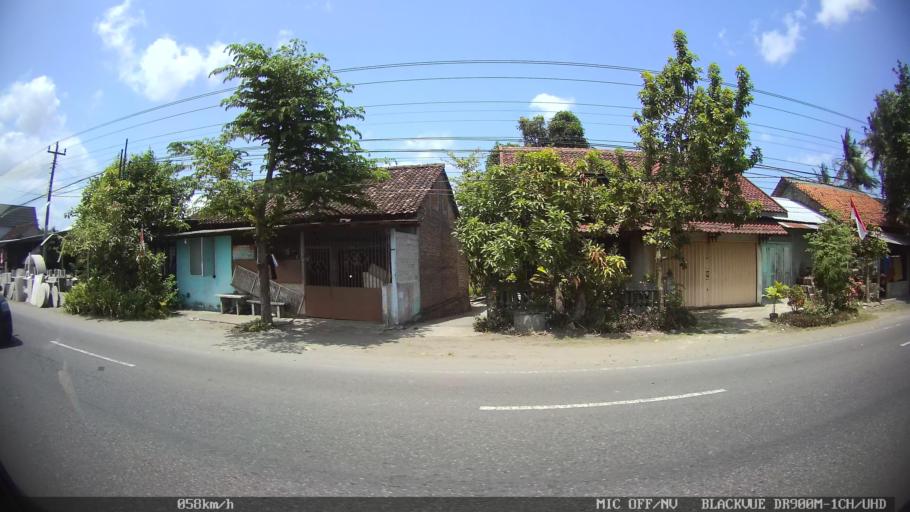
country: ID
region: Daerah Istimewa Yogyakarta
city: Pandak
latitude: -7.9071
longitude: 110.3068
